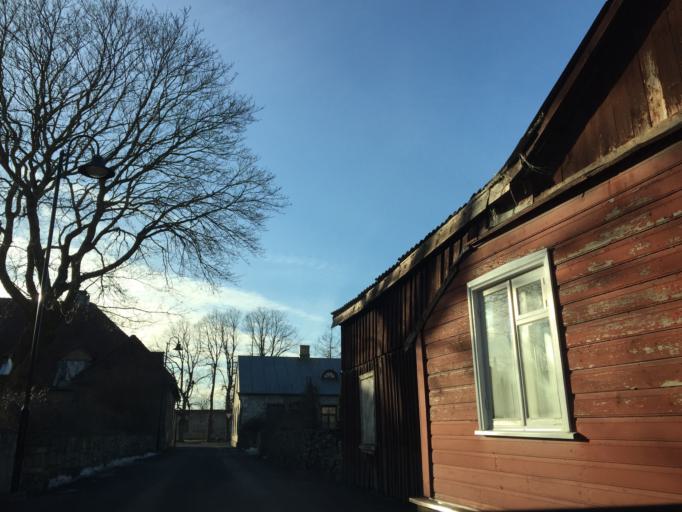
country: EE
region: Saare
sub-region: Kuressaare linn
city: Kuressaare
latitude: 58.2558
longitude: 22.4826
